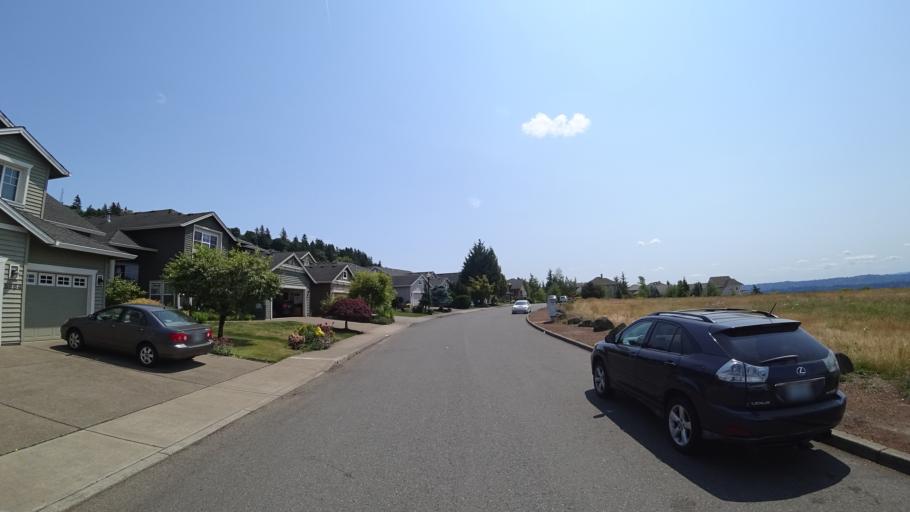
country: US
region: Oregon
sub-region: Multnomah County
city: Lents
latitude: 45.4577
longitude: -122.5590
